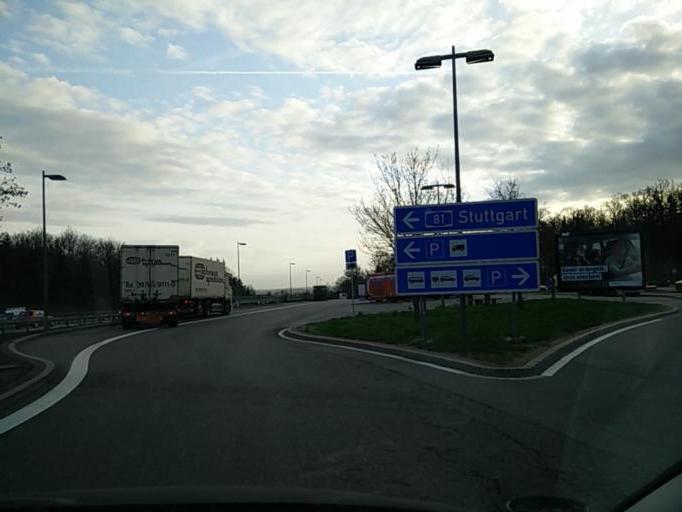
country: DE
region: Baden-Wuerttemberg
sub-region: Regierungsbezirk Stuttgart
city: Nufringen
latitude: 48.6155
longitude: 8.9065
